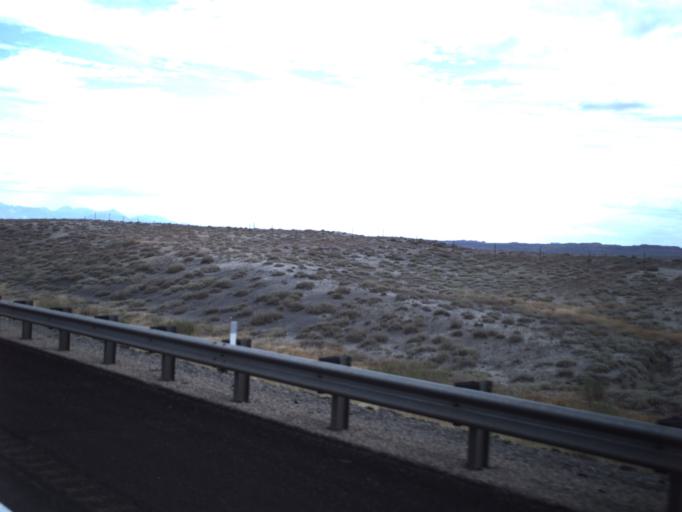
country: US
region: Utah
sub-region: Grand County
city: Moab
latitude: 38.9549
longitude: -109.7053
